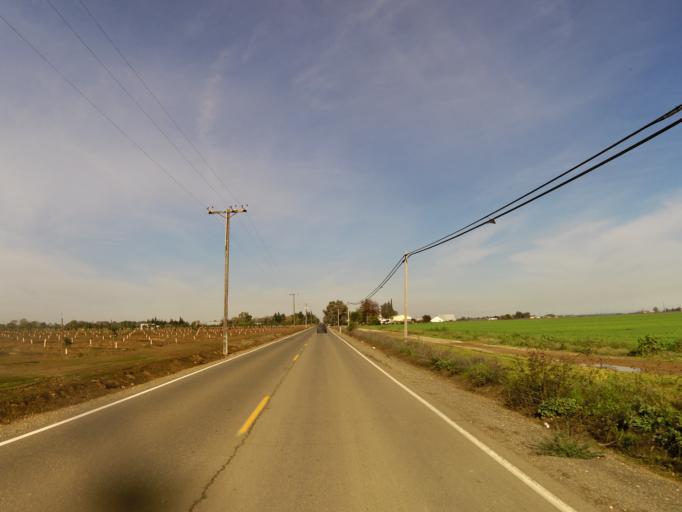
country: US
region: California
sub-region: Sacramento County
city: Elk Grove
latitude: 38.3289
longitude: -121.4172
